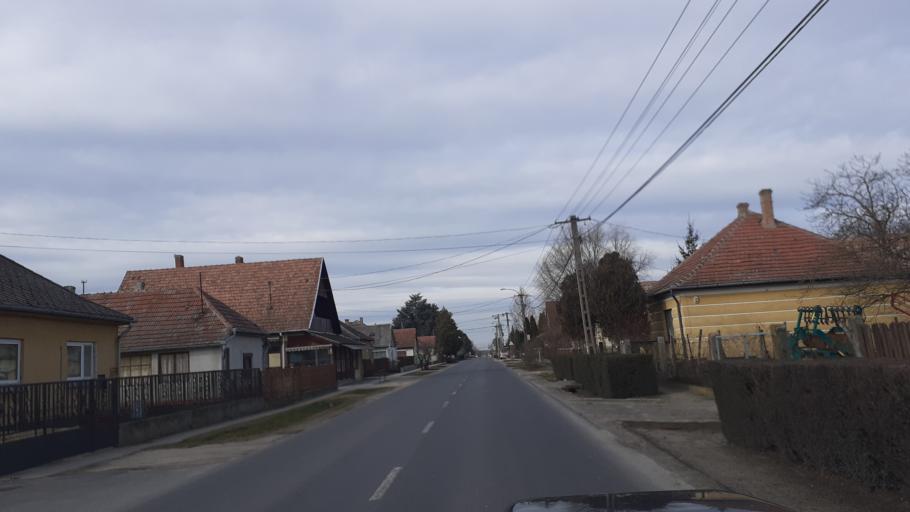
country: HU
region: Fejer
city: Sarbogard
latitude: 46.9002
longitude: 18.6031
